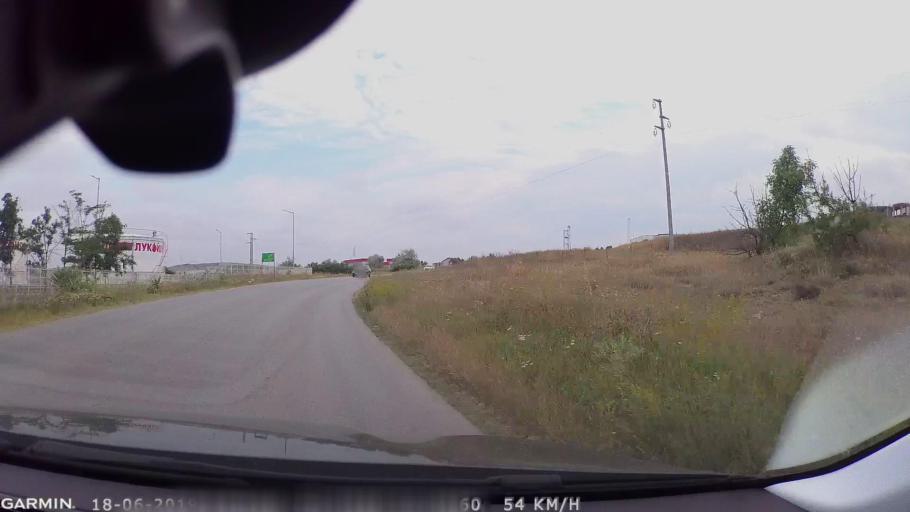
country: MK
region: Stip
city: Shtip
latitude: 41.7727
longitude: 22.1826
